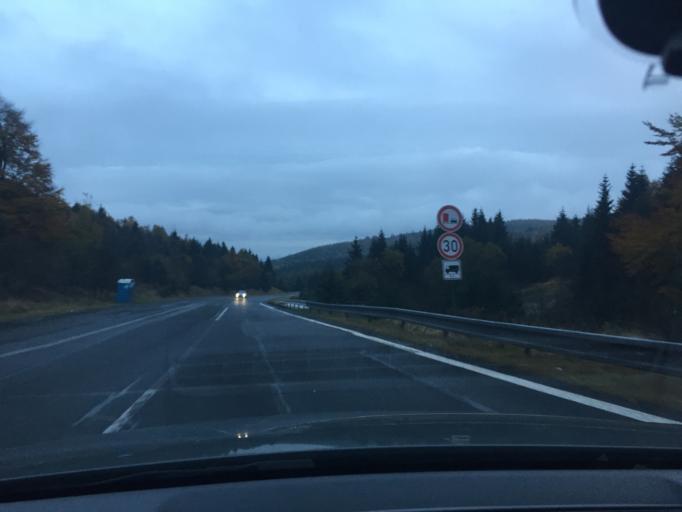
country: DE
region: Saxony
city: Altenberg
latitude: 50.7239
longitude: 13.7572
